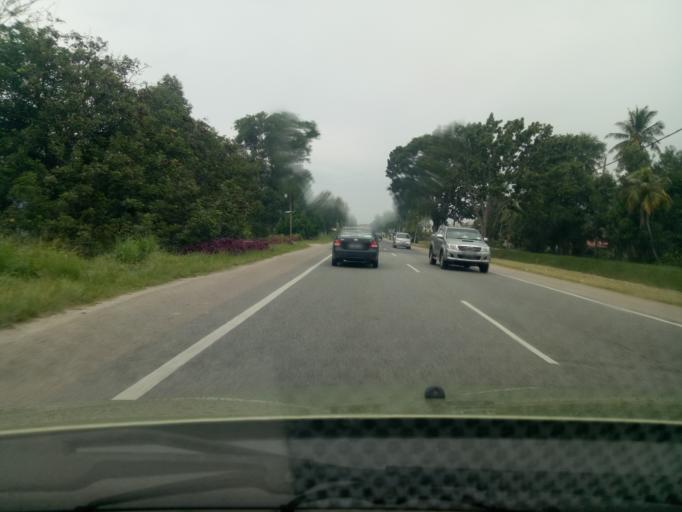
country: MY
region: Kedah
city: Gurun
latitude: 5.8787
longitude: 100.4481
